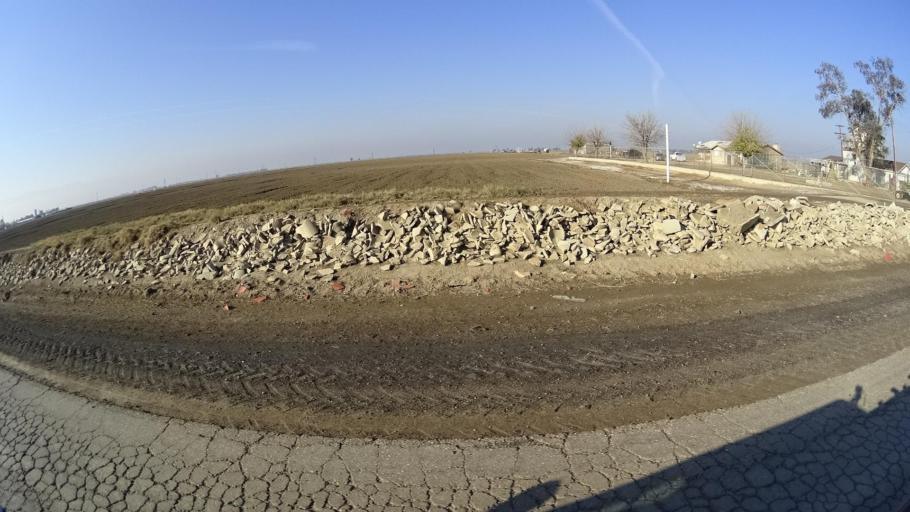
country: US
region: California
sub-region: Kern County
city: Weedpatch
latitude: 35.1684
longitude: -118.9677
